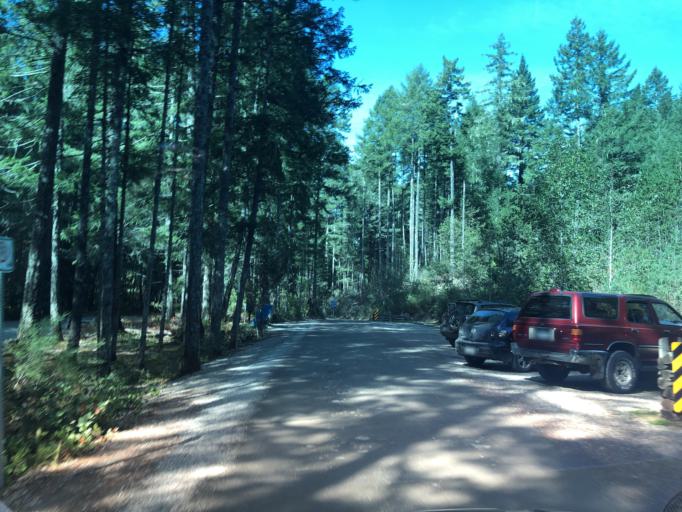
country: CA
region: British Columbia
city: Sooke
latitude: 48.4429
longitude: -123.7206
